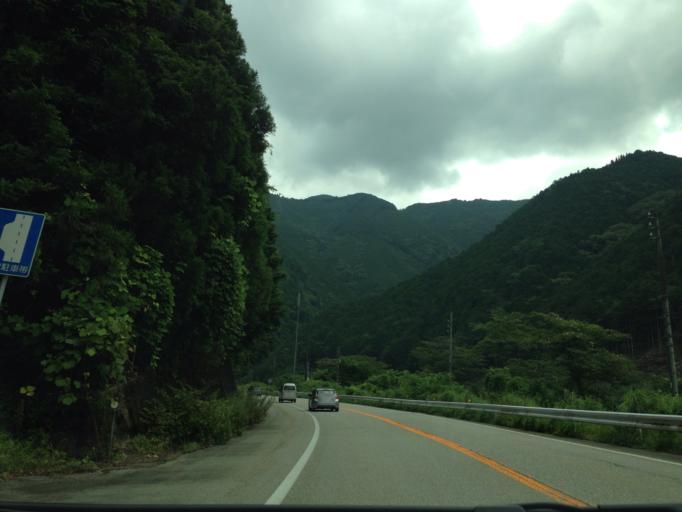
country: JP
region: Gifu
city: Gujo
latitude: 35.7519
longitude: 137.2249
